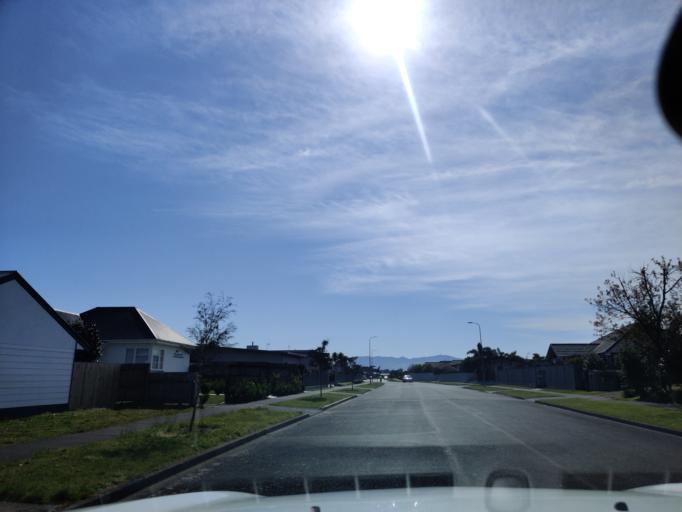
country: NZ
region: Manawatu-Wanganui
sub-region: Palmerston North City
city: Palmerston North
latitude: -40.3335
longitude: 175.6564
